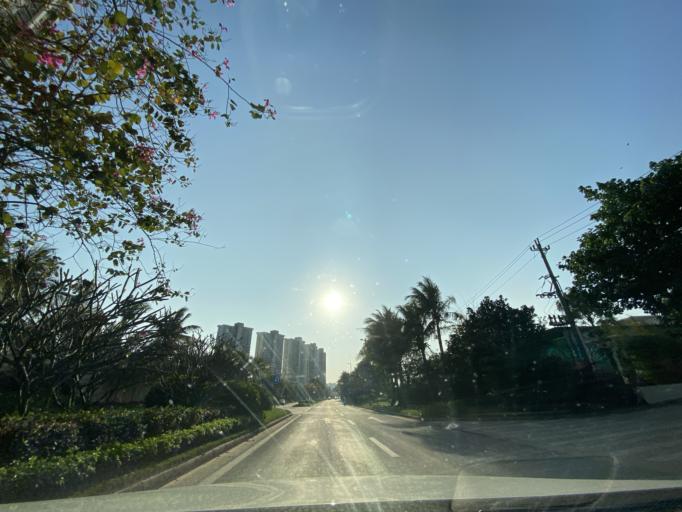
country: CN
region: Hainan
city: Xincun
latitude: 18.4222
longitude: 109.9236
